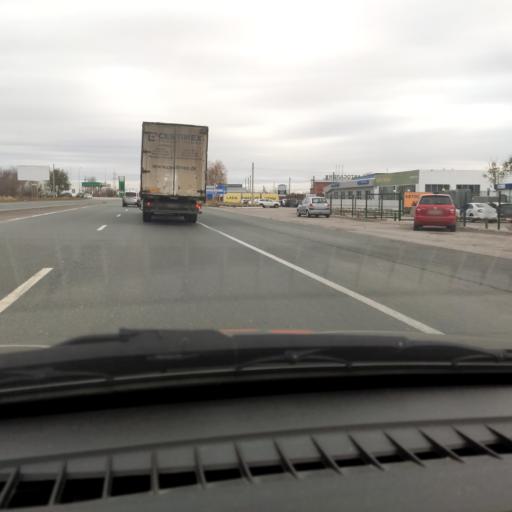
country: RU
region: Samara
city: Tol'yatti
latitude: 53.5768
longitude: 49.3984
